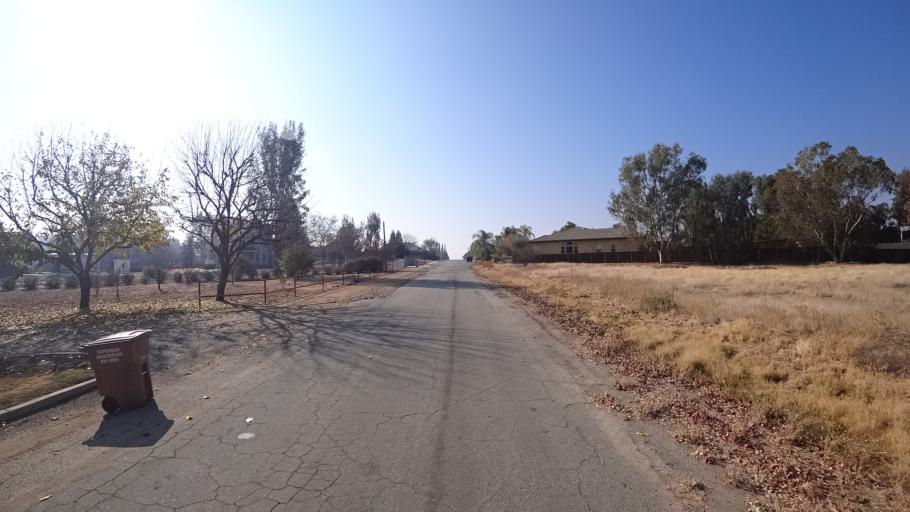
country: US
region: California
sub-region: Kern County
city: Oildale
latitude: 35.4076
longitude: -118.8670
